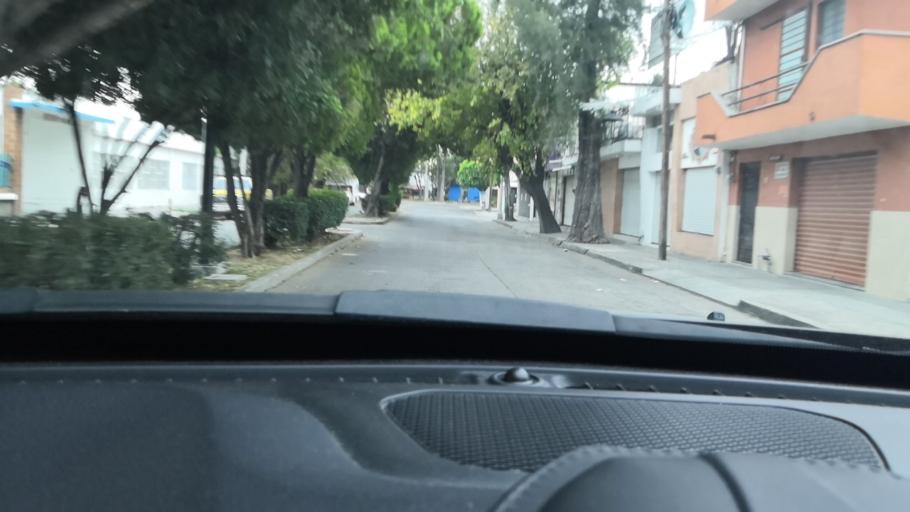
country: MX
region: Guanajuato
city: Leon
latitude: 21.1110
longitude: -101.6684
